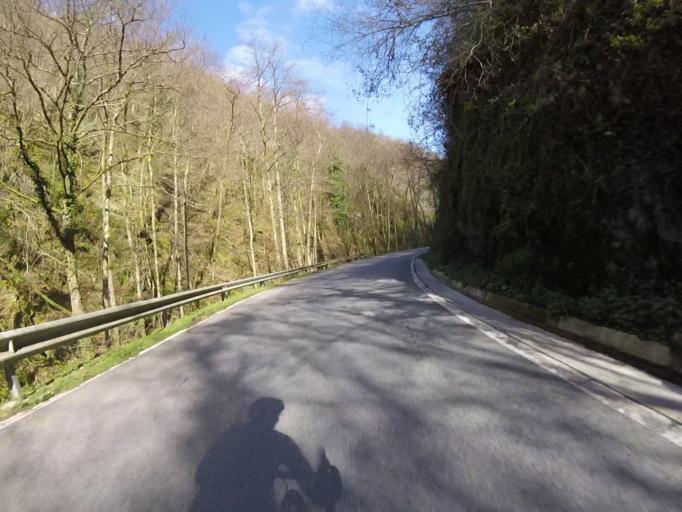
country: ES
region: Navarre
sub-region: Provincia de Navarra
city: Ezkurra
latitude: 43.1153
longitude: -1.8539
